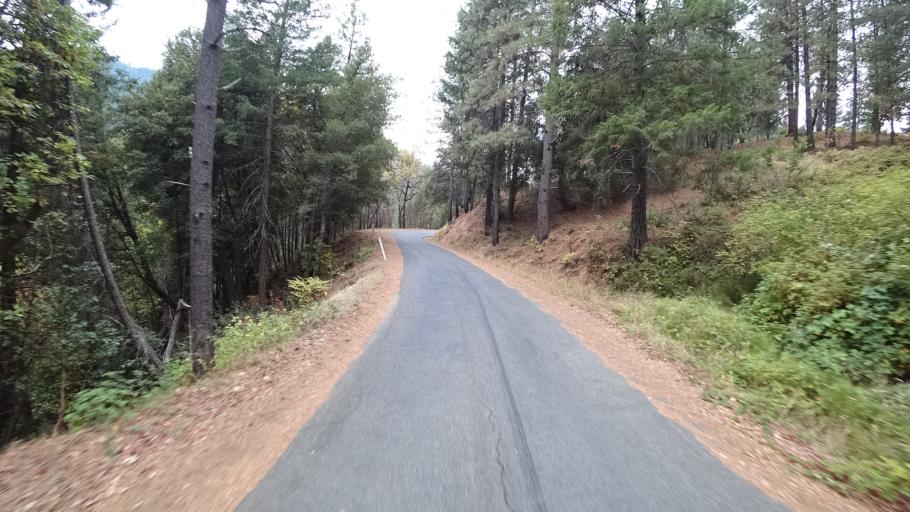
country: US
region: California
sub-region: Siskiyou County
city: Happy Camp
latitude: 41.7789
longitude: -123.3816
